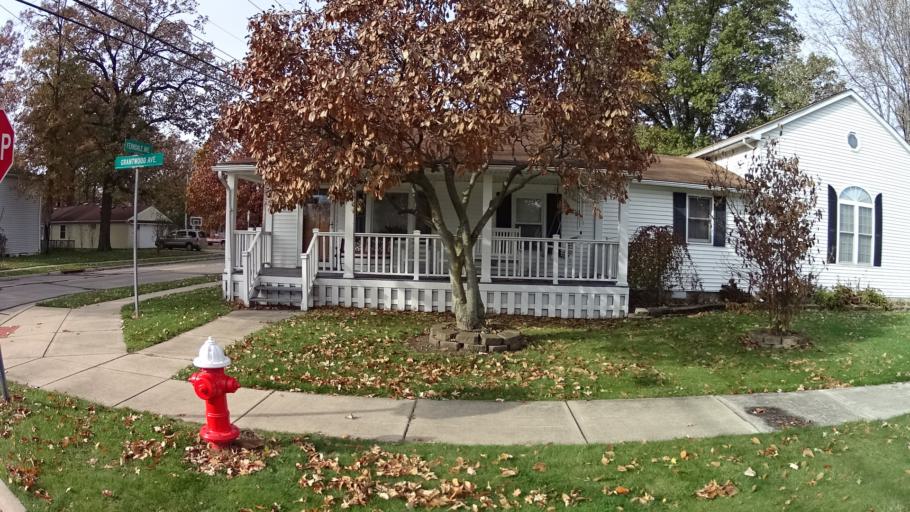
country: US
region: Ohio
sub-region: Lorain County
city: Sheffield Lake
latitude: 41.4851
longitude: -82.1049
